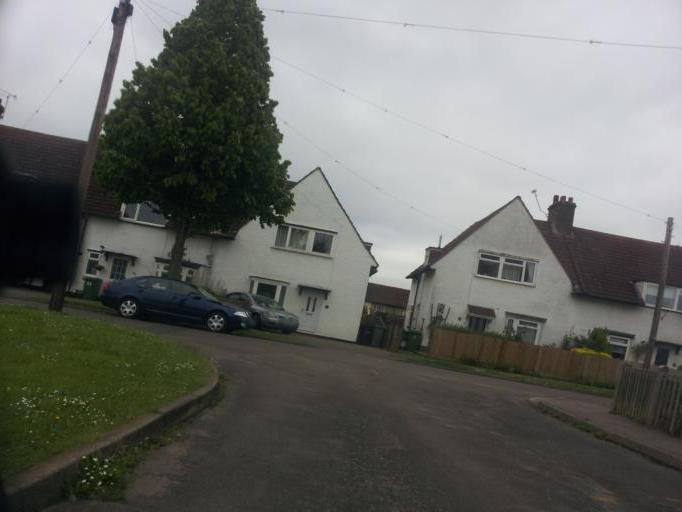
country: GB
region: England
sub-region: Kent
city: Maidstone
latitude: 51.2704
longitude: 0.4894
